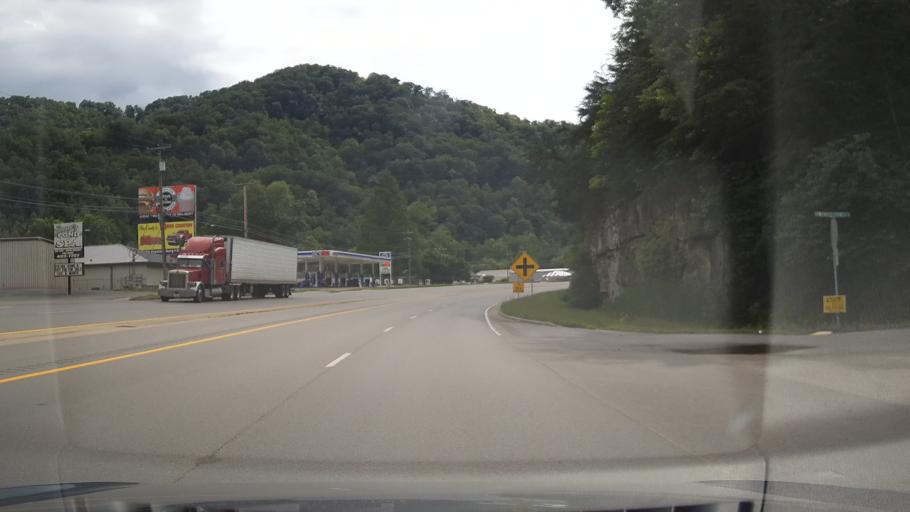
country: US
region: Kentucky
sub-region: Pike County
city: Pikeville
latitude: 37.4441
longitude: -82.5183
